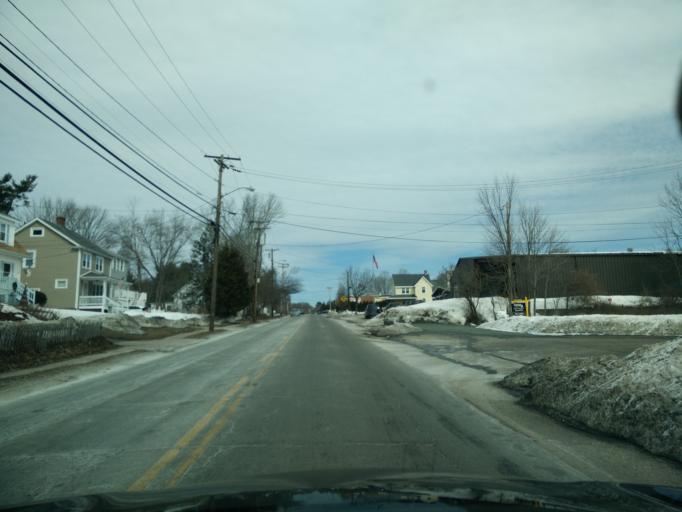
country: US
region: Massachusetts
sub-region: Norfolk County
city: Walpole
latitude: 42.1552
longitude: -71.2453
